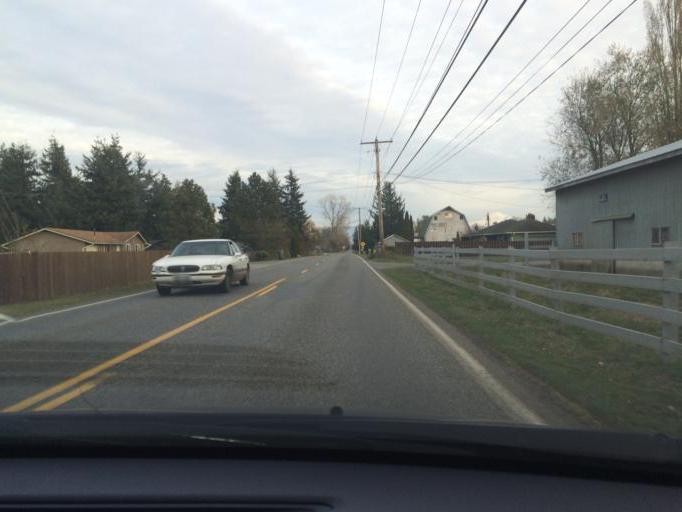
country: US
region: Washington
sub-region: Whatcom County
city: Ferndale
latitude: 48.9061
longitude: -122.5786
